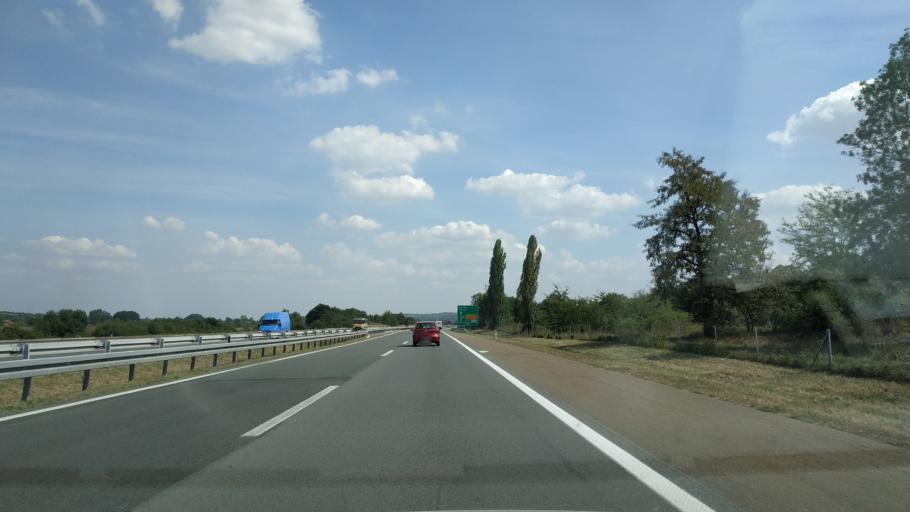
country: RS
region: Central Serbia
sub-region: Podunavski Okrug
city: Smederevo
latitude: 44.5796
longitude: 20.8786
